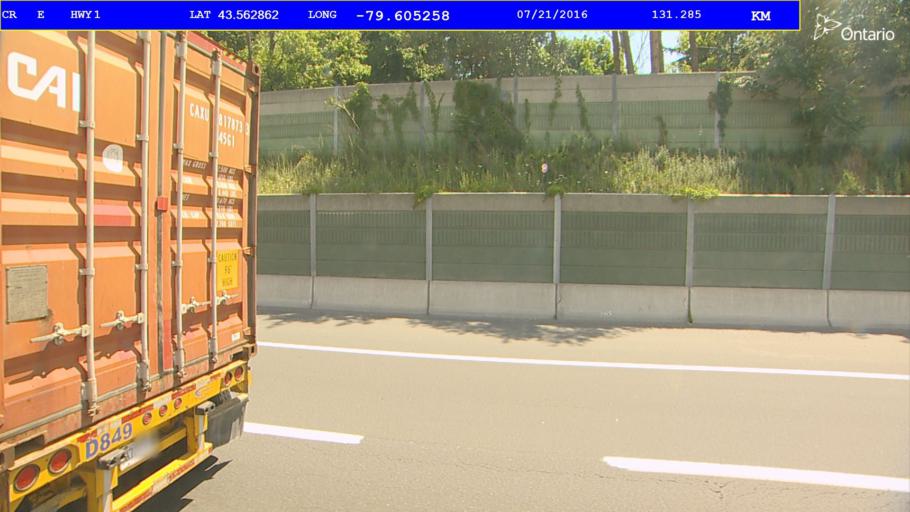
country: CA
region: Ontario
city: Mississauga
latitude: 43.5628
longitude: -79.6053
